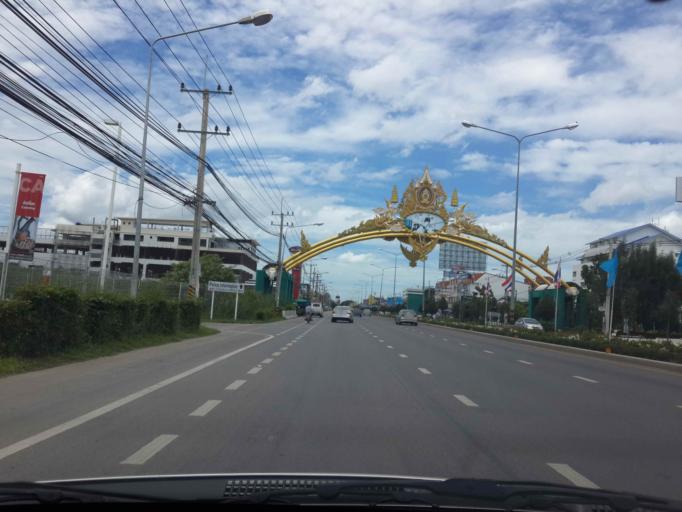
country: TH
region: Prachuap Khiri Khan
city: Hua Hin
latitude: 12.6208
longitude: 99.9505
